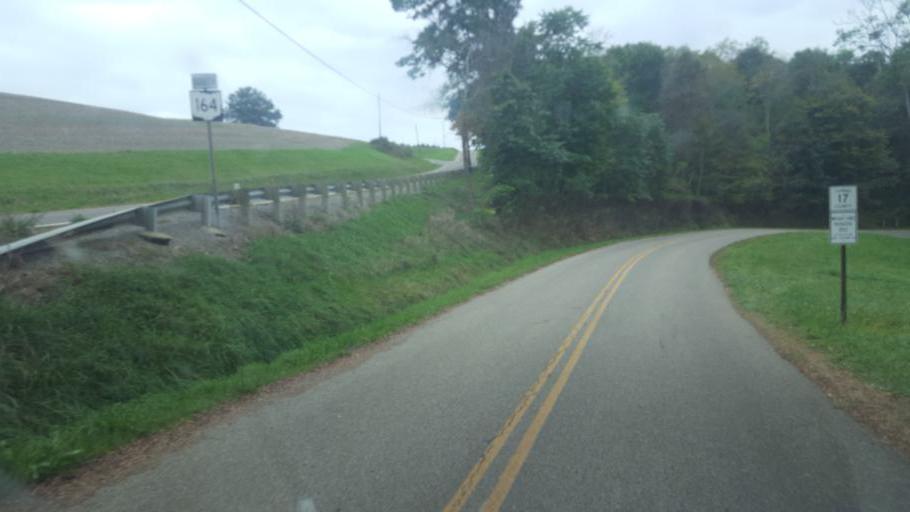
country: US
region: Ohio
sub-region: Carroll County
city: Carrollton
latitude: 40.4618
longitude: -81.0092
